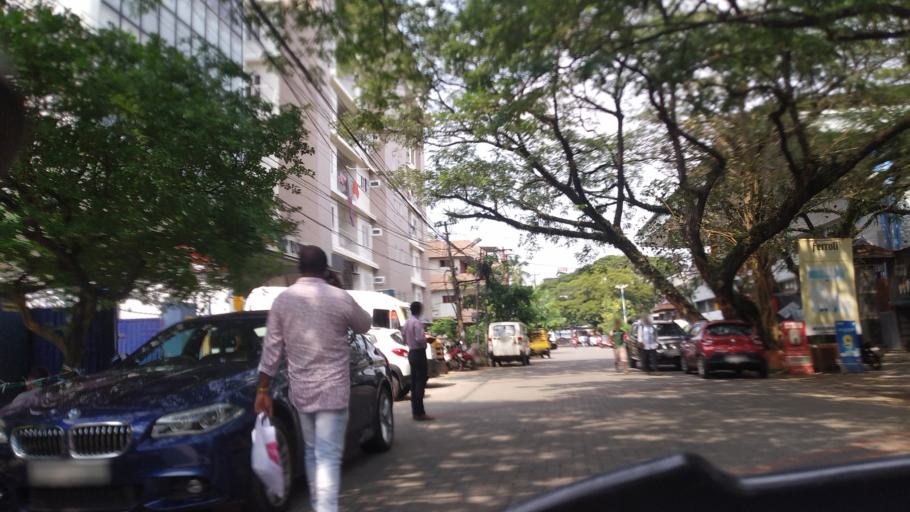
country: IN
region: Kerala
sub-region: Ernakulam
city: Cochin
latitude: 9.9733
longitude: 76.2833
